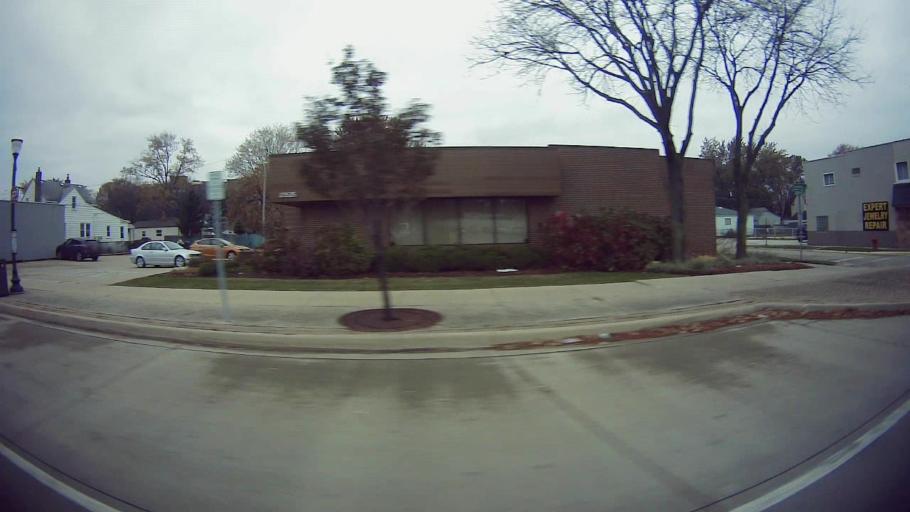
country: US
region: Michigan
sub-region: Oakland County
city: Hazel Park
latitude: 42.4646
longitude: -83.1041
